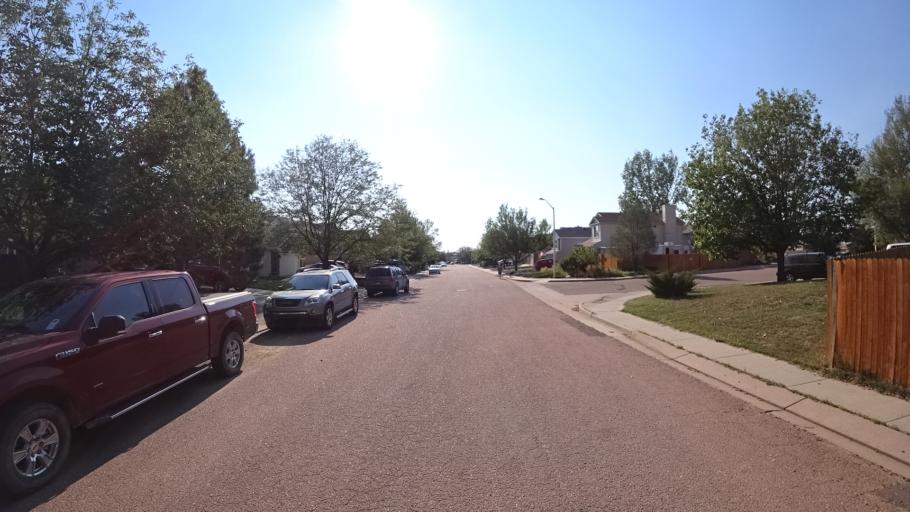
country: US
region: Colorado
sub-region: El Paso County
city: Stratmoor
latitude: 38.7739
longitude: -104.8060
